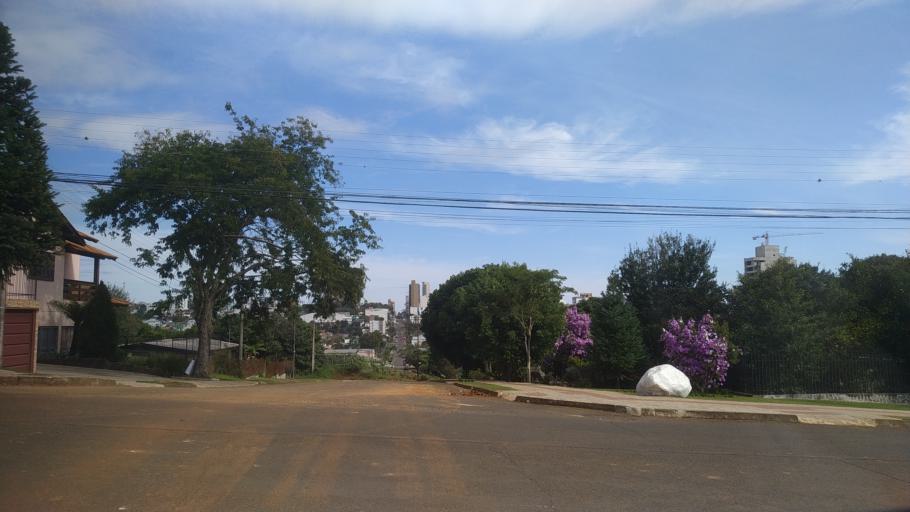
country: BR
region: Santa Catarina
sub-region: Chapeco
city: Chapeco
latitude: -27.1077
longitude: -52.6008
